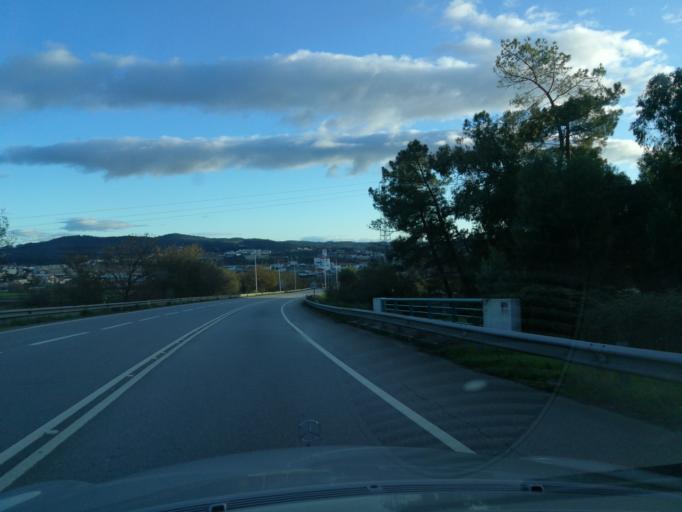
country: PT
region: Braga
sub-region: Barcelos
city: Vila Frescainha
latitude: 41.5385
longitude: -8.6393
